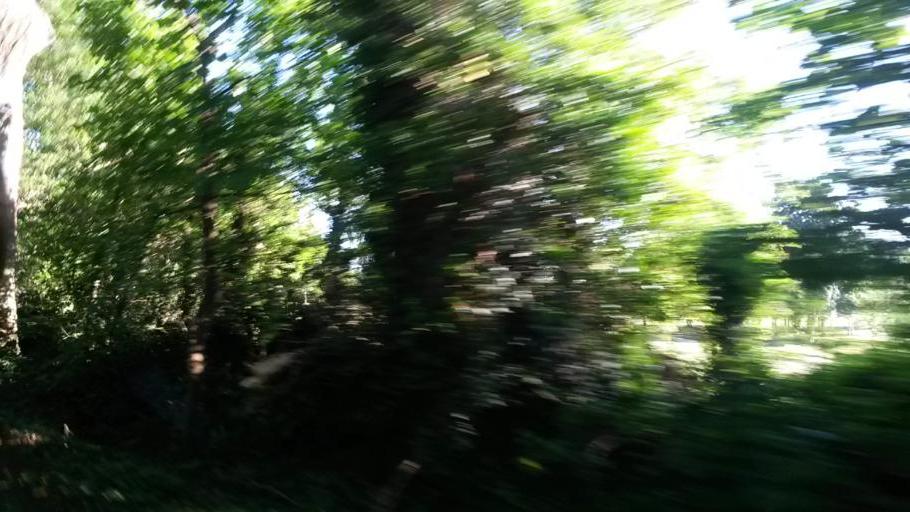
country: IE
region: Leinster
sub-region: Dublin City
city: Finglas
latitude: 53.4582
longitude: -6.3216
